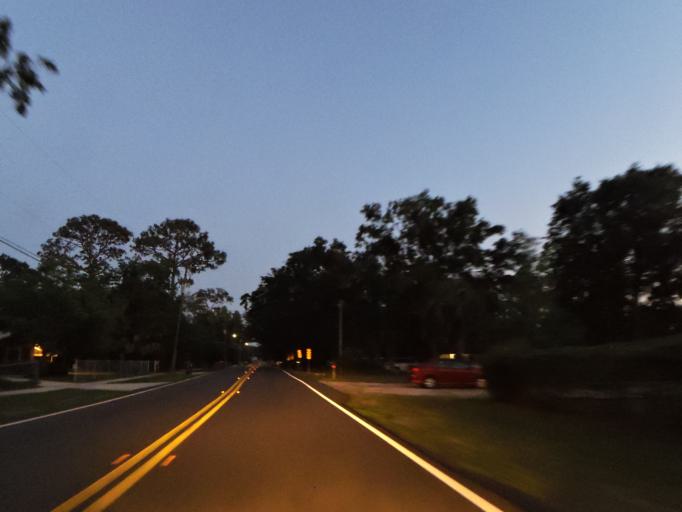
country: US
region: Florida
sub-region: Duval County
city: Jacksonville
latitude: 30.2948
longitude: -81.5408
